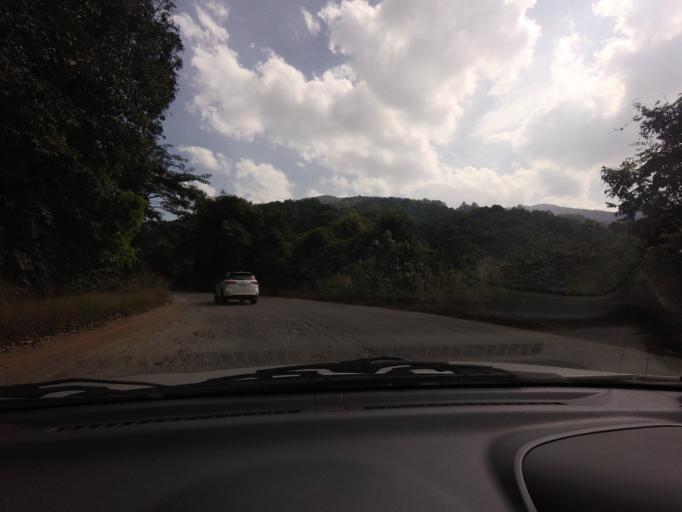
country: IN
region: Karnataka
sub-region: Hassan
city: Sakleshpur
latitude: 12.8281
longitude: 75.6401
